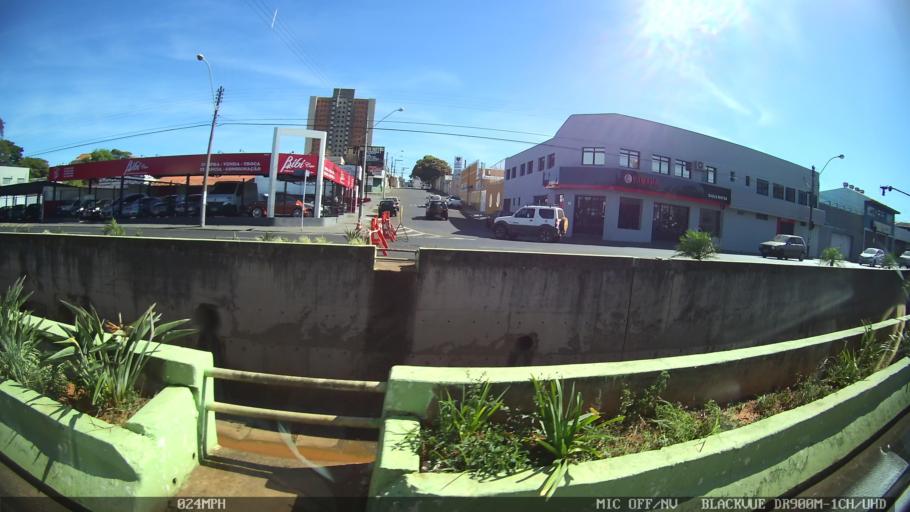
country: BR
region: Sao Paulo
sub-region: Franca
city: Franca
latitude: -20.5295
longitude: -47.4034
